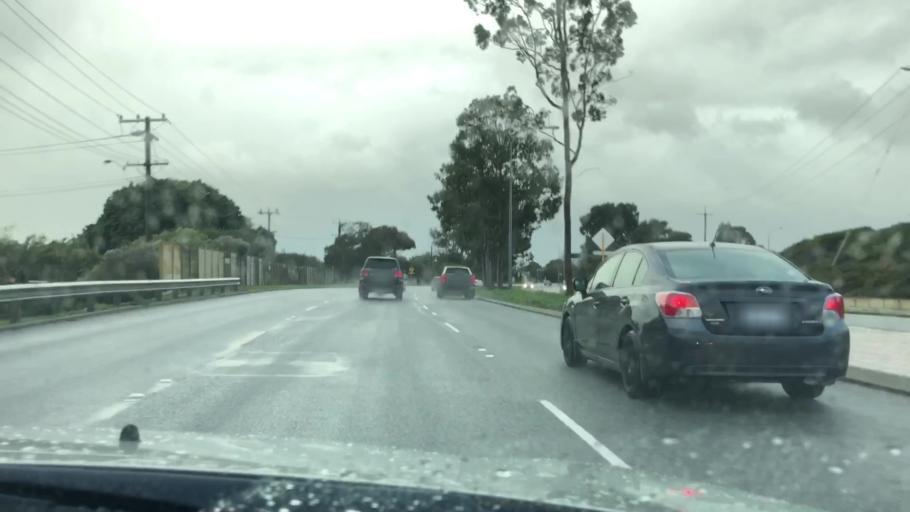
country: AU
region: Western Australia
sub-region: Canning
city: Willetton
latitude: -32.0667
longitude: 115.8819
